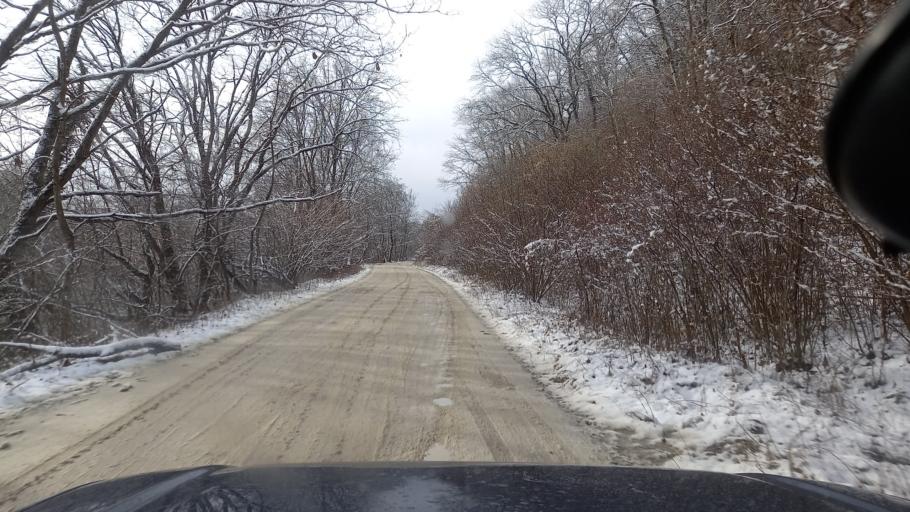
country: RU
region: Adygeya
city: Kamennomostskiy
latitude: 44.2398
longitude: 40.1956
